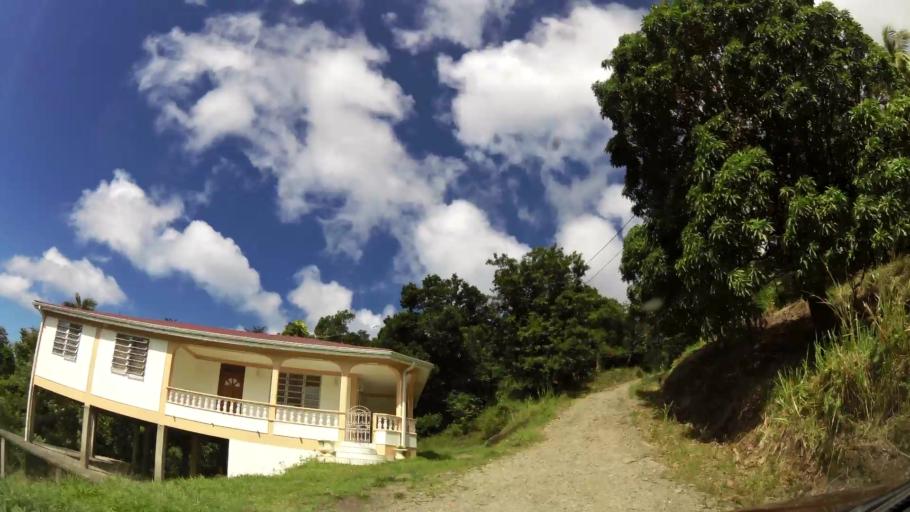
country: DM
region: Saint John
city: Portsmouth
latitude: 15.6066
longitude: -61.4595
